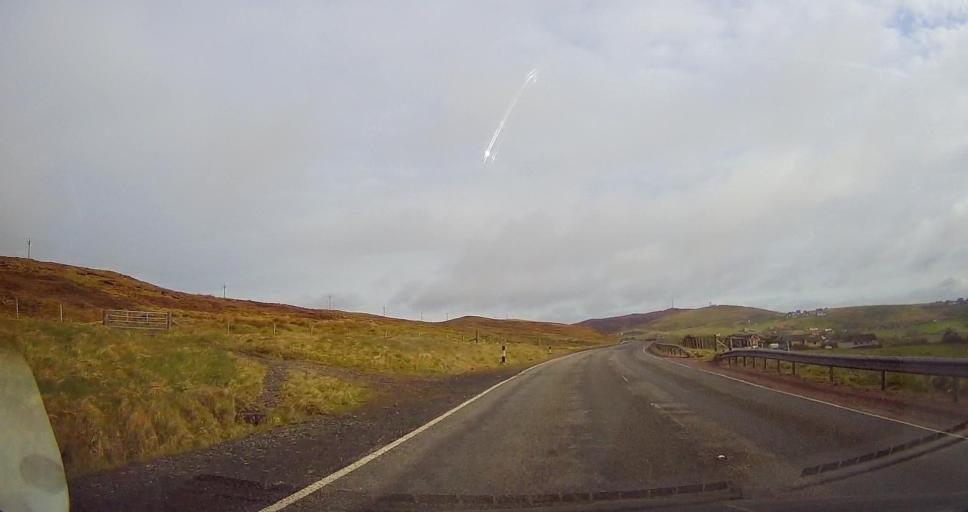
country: GB
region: Scotland
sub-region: Shetland Islands
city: Lerwick
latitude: 60.1246
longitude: -1.2173
